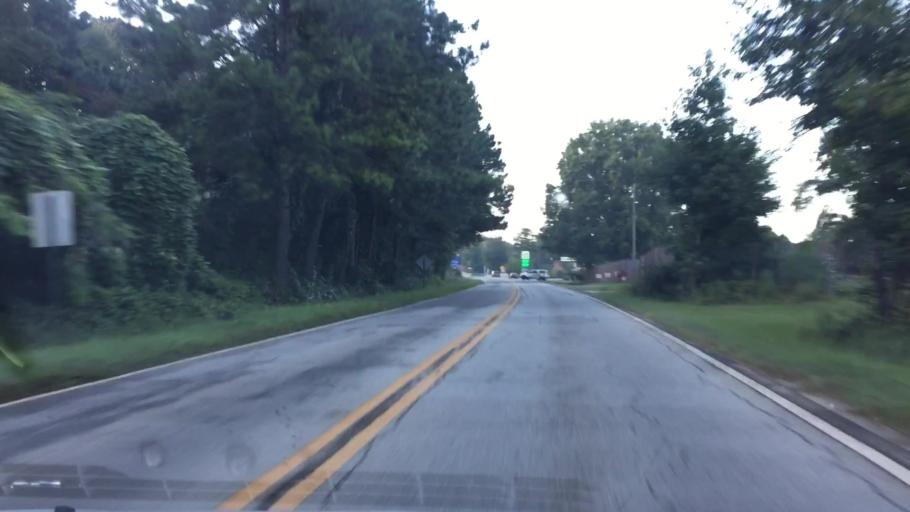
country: US
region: Georgia
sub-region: Clayton County
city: Lovejoy
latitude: 33.4230
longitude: -84.2847
